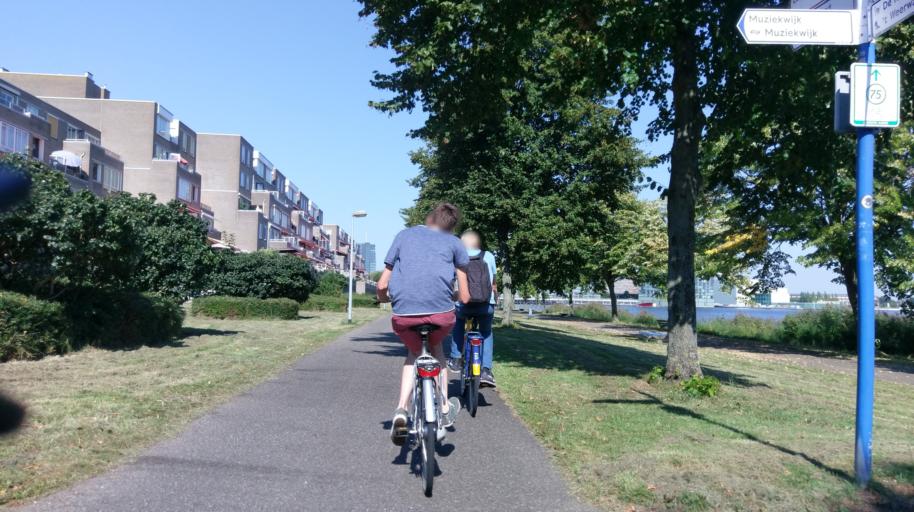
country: NL
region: Flevoland
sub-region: Gemeente Almere
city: Almere Stad
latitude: 52.3626
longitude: 5.2117
